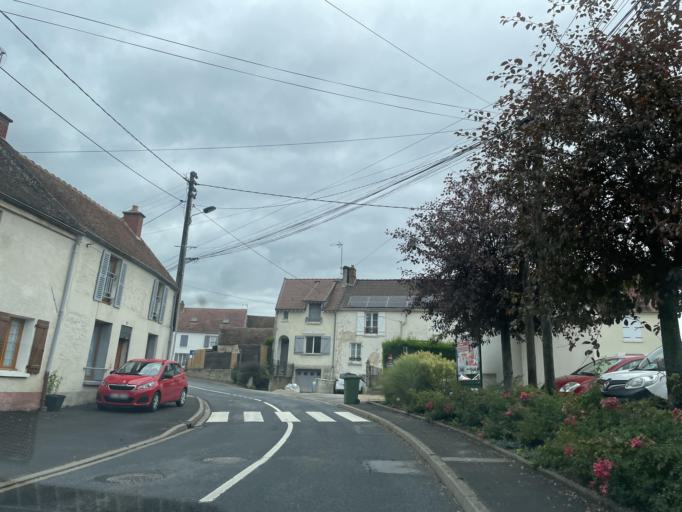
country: FR
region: Ile-de-France
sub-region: Departement de Seine-et-Marne
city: Chailly-en-Brie
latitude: 48.8125
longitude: 3.1113
